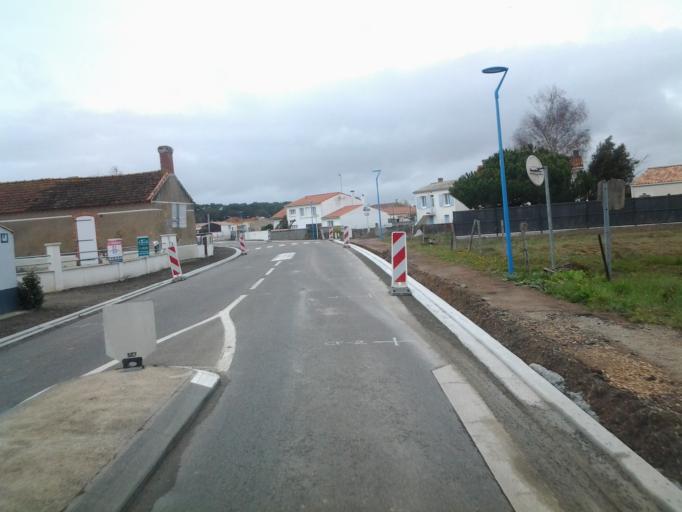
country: FR
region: Pays de la Loire
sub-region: Departement de la Vendee
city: Longeville-sur-Mer
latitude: 46.3852
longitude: -1.4666
